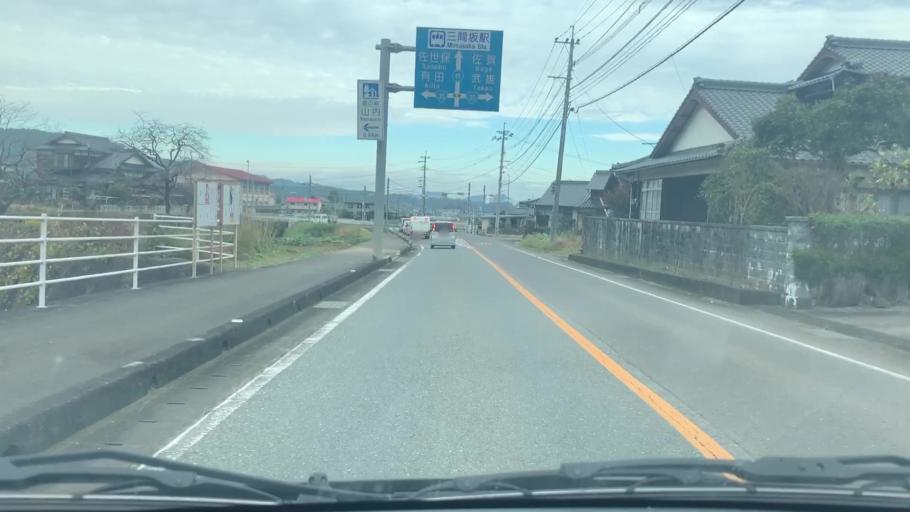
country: JP
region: Saga Prefecture
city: Takeocho-takeo
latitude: 33.1911
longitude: 129.9655
